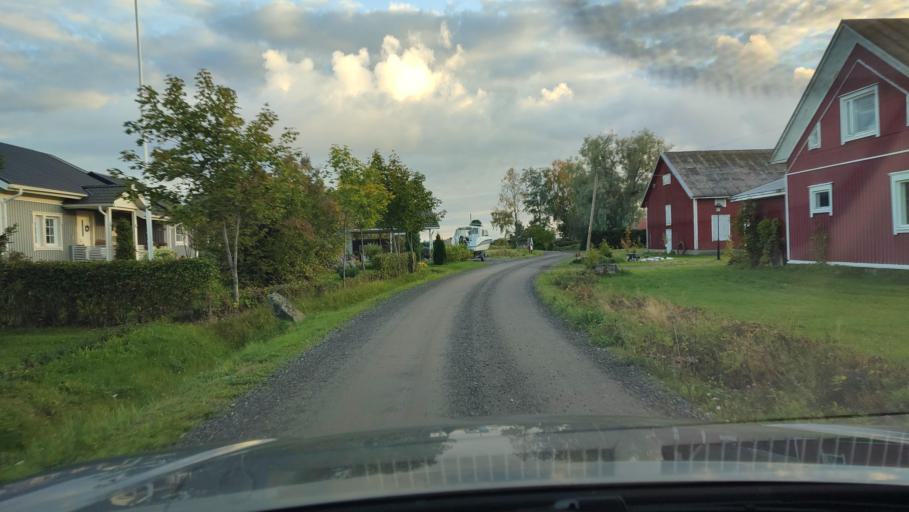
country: FI
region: Ostrobothnia
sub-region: Sydosterbotten
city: Kristinestad
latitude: 62.2511
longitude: 21.5122
